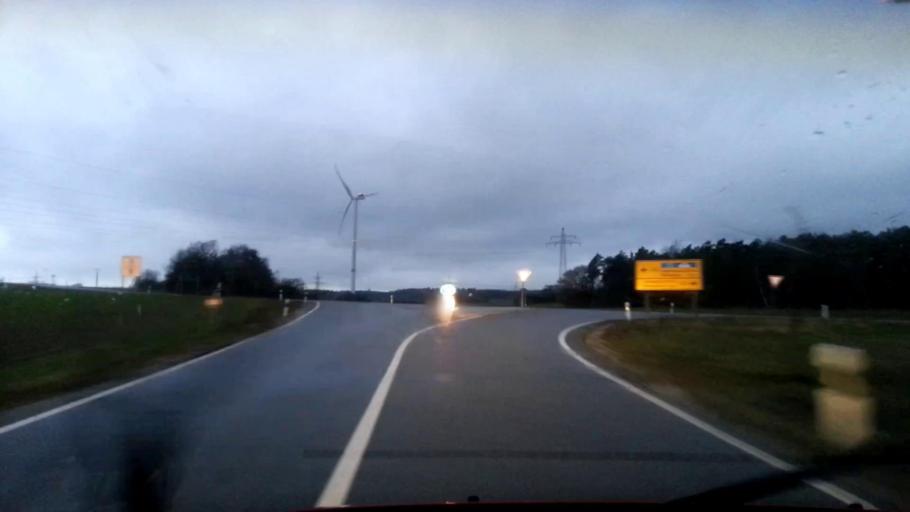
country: DE
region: Bavaria
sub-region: Upper Franconia
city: Poxdorf
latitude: 49.9736
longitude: 11.1200
